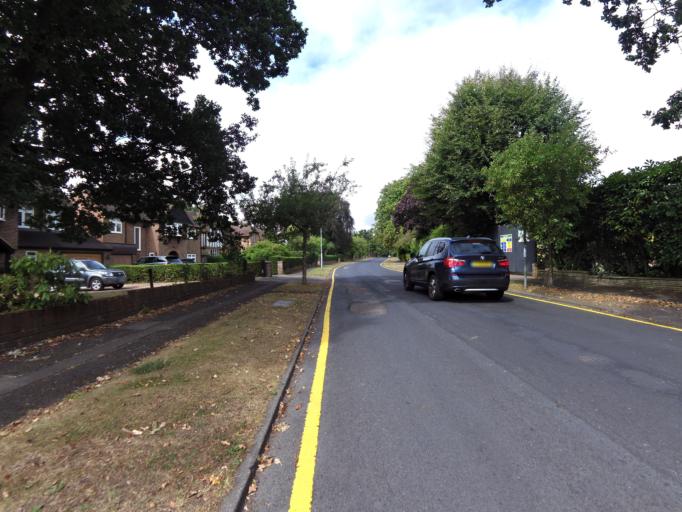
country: GB
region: England
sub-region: Hertfordshire
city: Radlett
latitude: 51.6854
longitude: -0.3094
